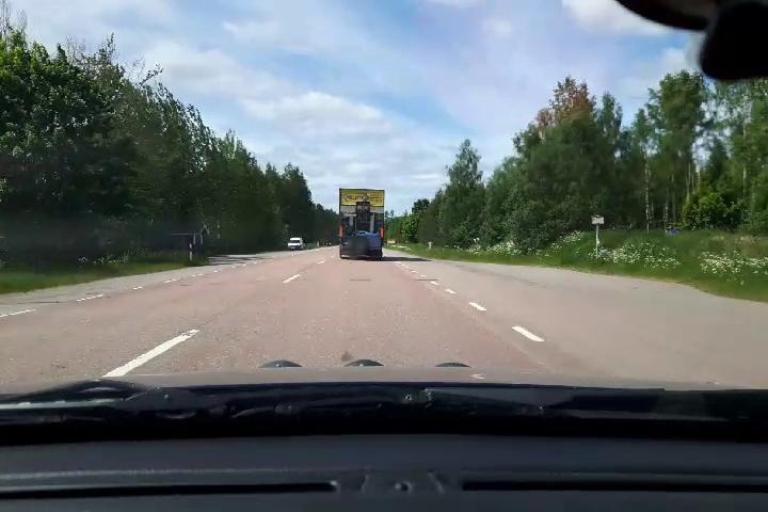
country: SE
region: Uppsala
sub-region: Osthammars Kommun
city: Bjorklinge
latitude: 60.1102
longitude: 17.5339
